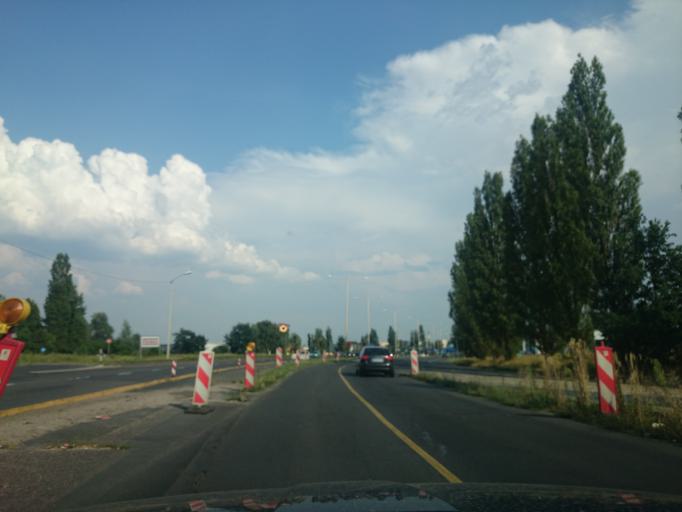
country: PL
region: West Pomeranian Voivodeship
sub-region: Szczecin
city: Szczecin
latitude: 53.3868
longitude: 14.6391
